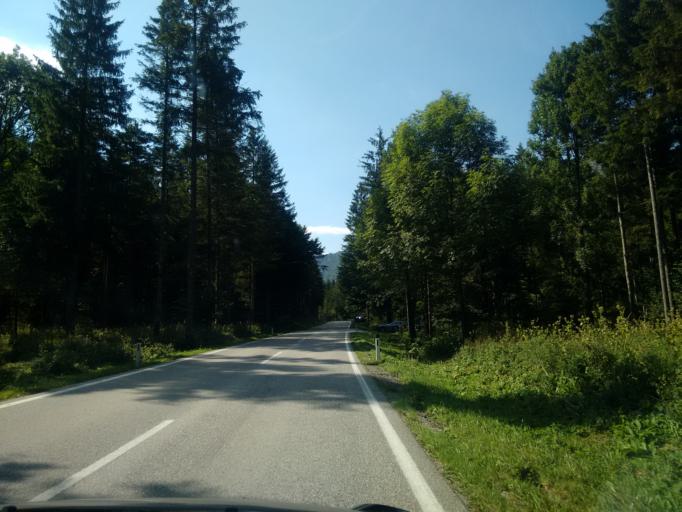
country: AT
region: Upper Austria
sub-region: Politischer Bezirk Gmunden
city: Gruenau im Almtal
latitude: 47.8114
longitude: 13.9525
